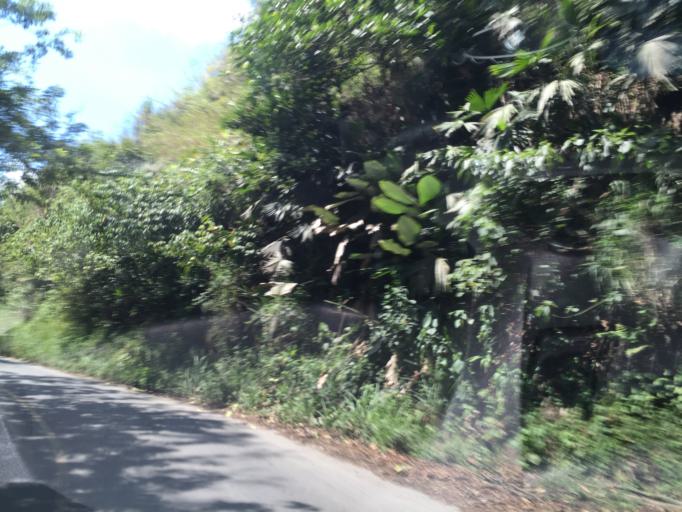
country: CO
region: Valle del Cauca
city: Ulloa
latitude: 4.7462
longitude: -75.7815
